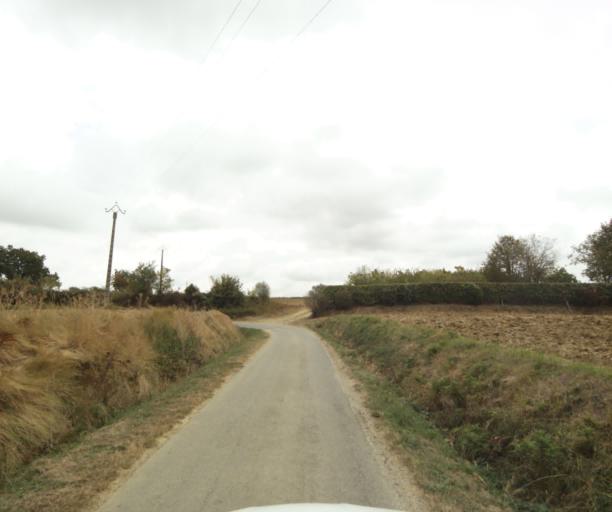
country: FR
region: Midi-Pyrenees
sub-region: Departement de la Haute-Garonne
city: Villefranche-de-Lauragais
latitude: 43.4118
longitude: 1.7192
